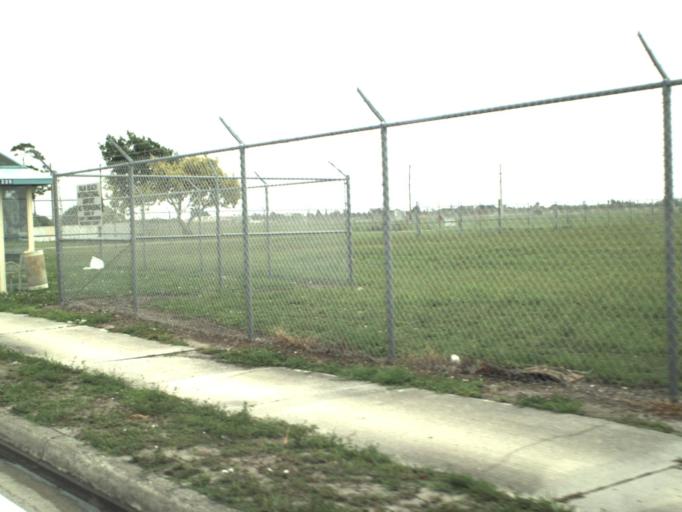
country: US
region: Florida
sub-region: Palm Beach County
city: Haverhill
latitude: 26.6852
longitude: -80.1117
